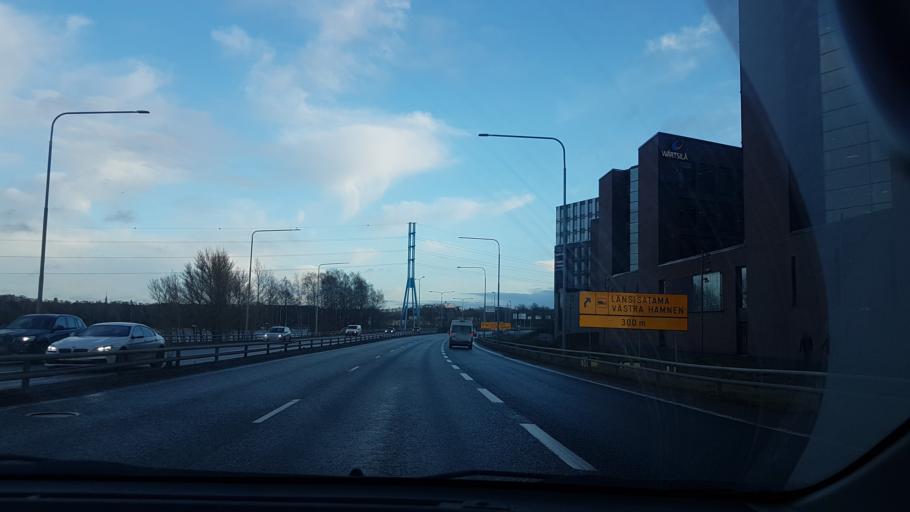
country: FI
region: Uusimaa
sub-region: Helsinki
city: Helsinki
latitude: 60.1667
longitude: 24.8999
